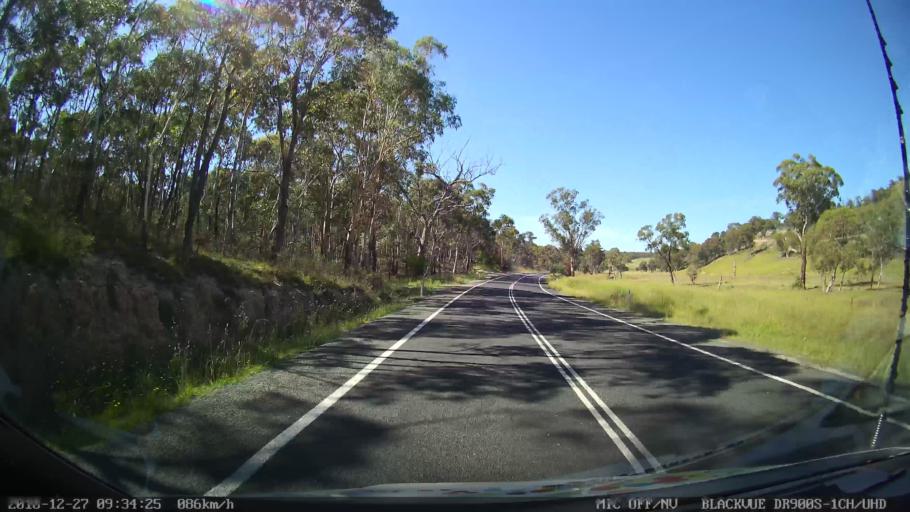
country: AU
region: New South Wales
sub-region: Lithgow
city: Portland
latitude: -33.2260
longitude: 150.0278
